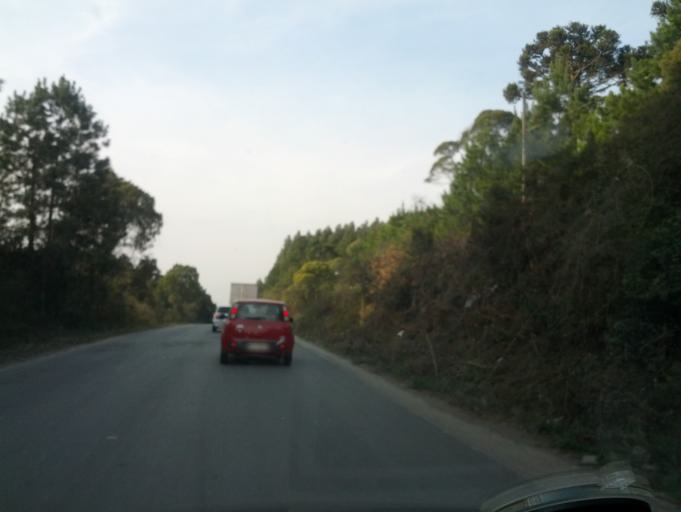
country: BR
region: Santa Catarina
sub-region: Otacilio Costa
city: Otacilio Costa
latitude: -27.5307
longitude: -50.1409
